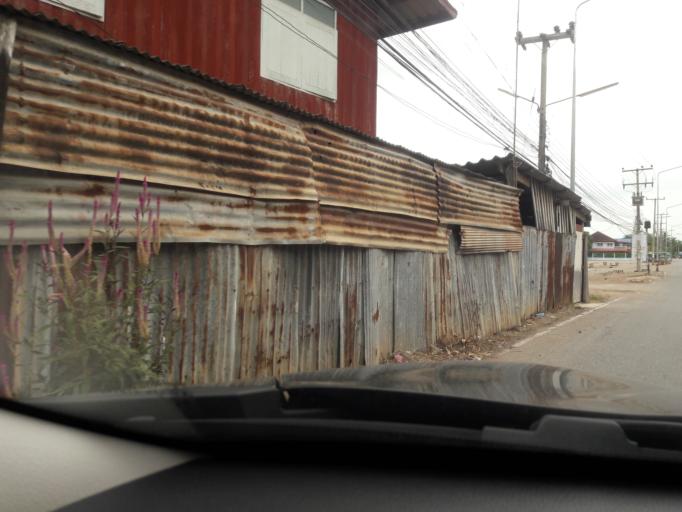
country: TH
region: Ratchaburi
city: Damnoen Saduak
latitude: 13.5905
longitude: 99.9408
